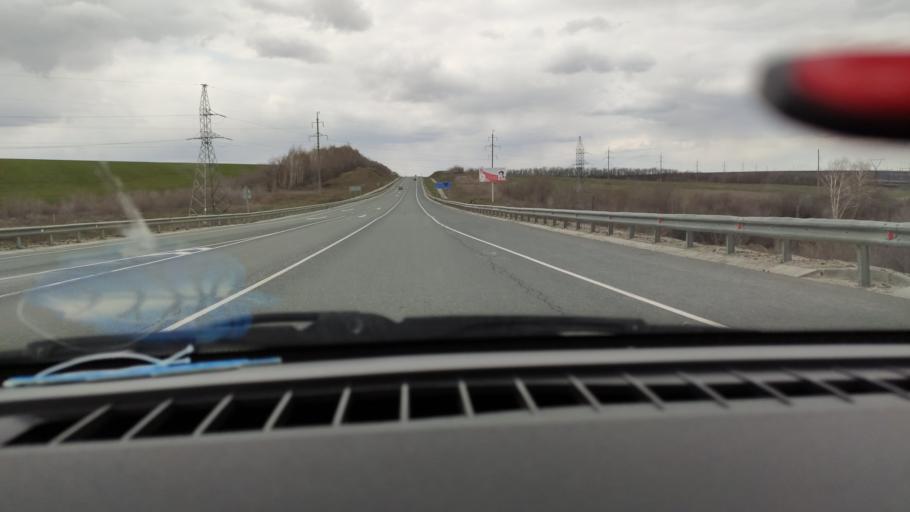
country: RU
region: Saratov
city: Shikhany
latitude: 52.1159
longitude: 47.2896
